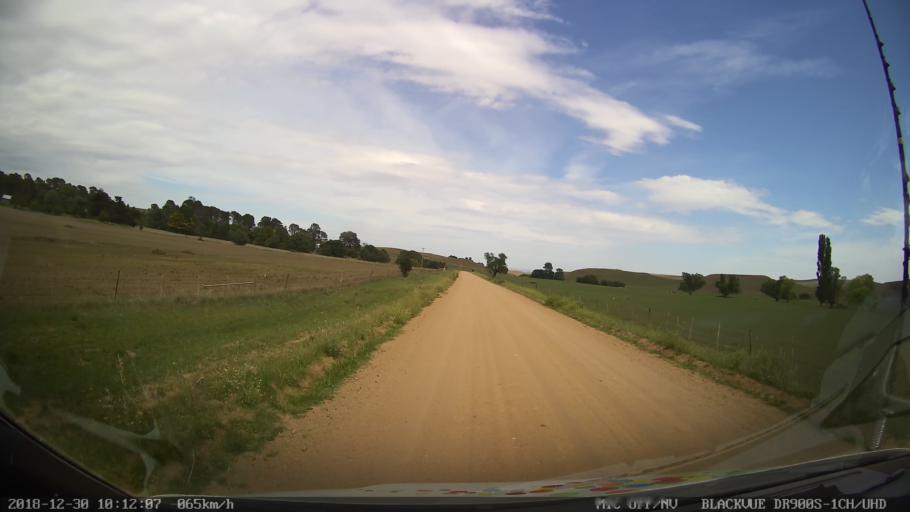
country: AU
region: New South Wales
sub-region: Snowy River
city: Berridale
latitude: -36.5433
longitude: 149.0788
